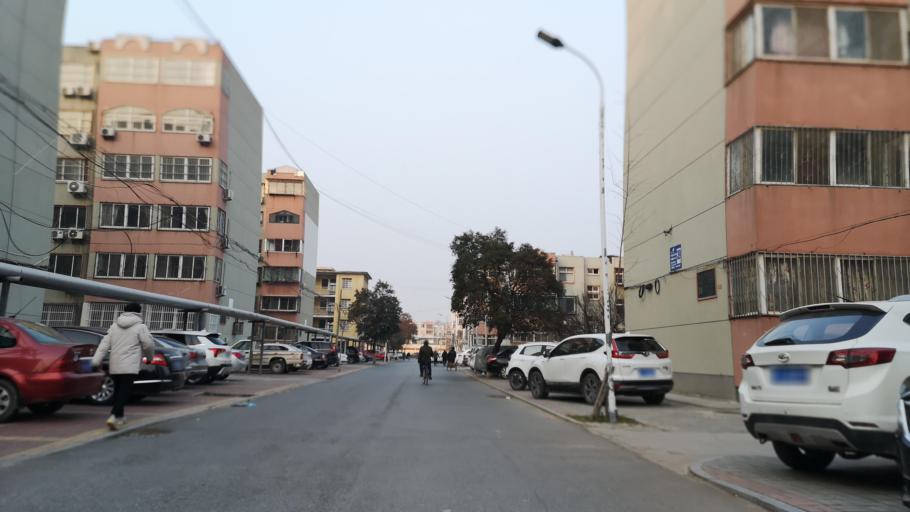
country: CN
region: Henan Sheng
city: Zhongyuanlu
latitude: 35.7670
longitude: 115.1005
